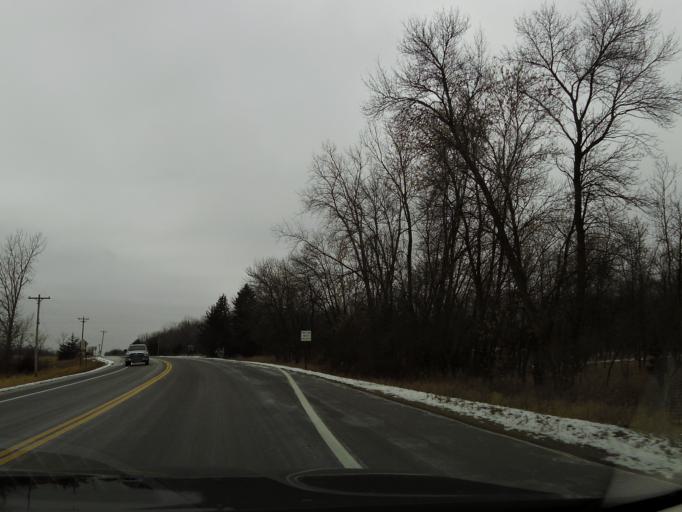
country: US
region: Minnesota
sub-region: Hennepin County
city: Medina
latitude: 45.0222
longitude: -93.6027
